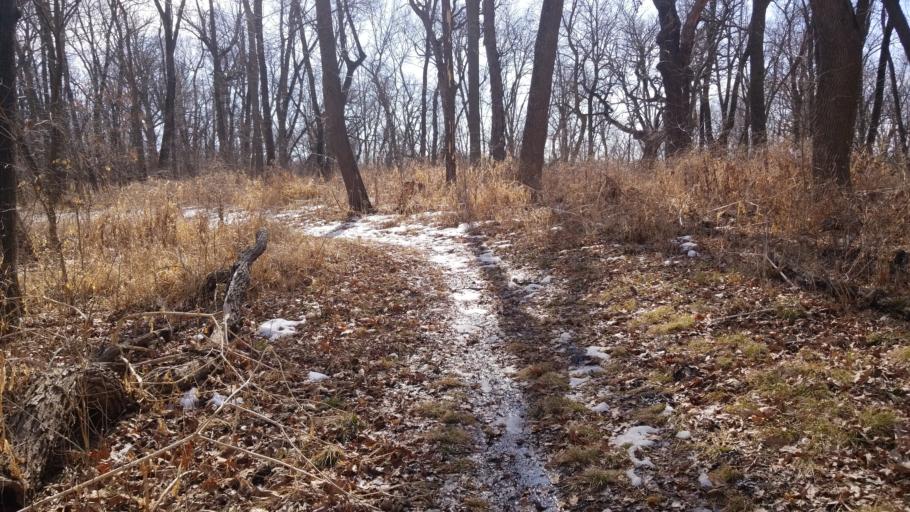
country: US
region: Nebraska
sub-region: Sarpy County
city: Bellevue
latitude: 41.1755
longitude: -95.9021
